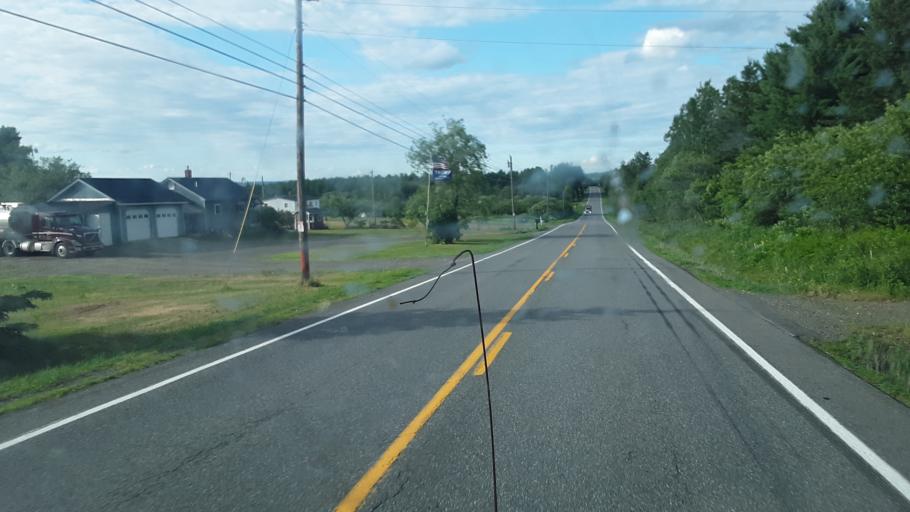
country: US
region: Maine
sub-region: Aroostook County
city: Presque Isle
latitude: 46.4874
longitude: -68.3791
